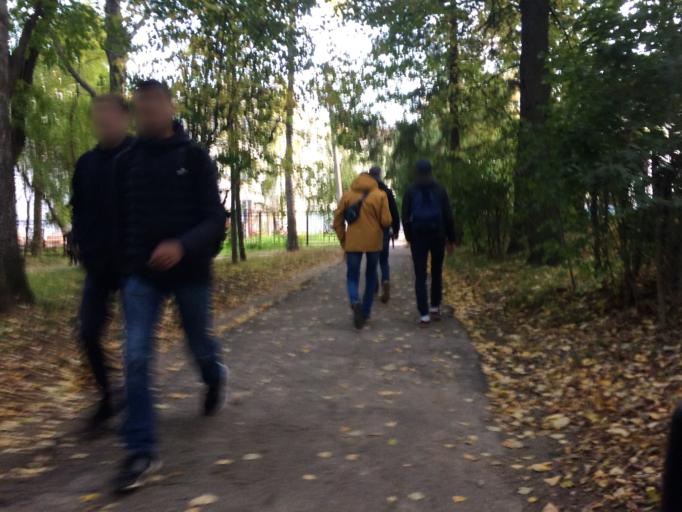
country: RU
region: Mariy-El
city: Yoshkar-Ola
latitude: 56.6349
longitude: 47.8892
